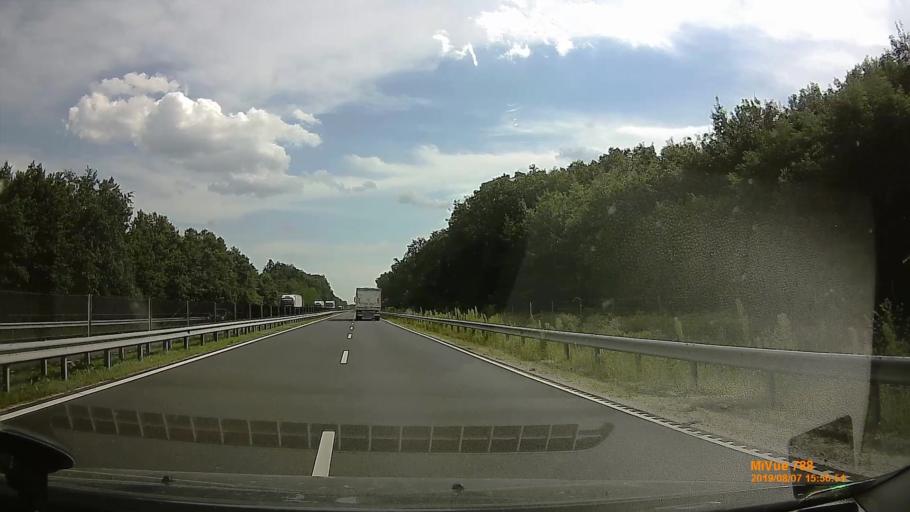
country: HU
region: Vas
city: Kormend
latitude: 47.0538
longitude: 16.6147
